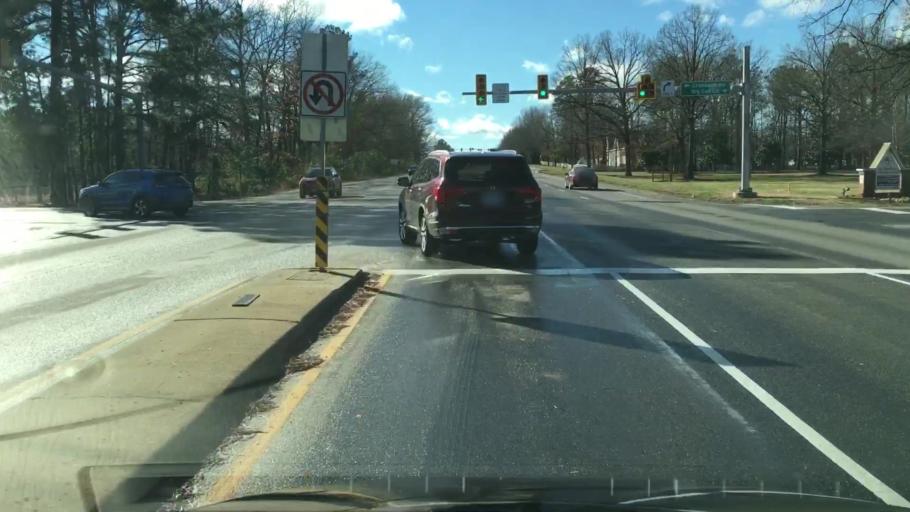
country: US
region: Virginia
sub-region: Chesterfield County
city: Bon Air
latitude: 37.5250
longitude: -77.6031
